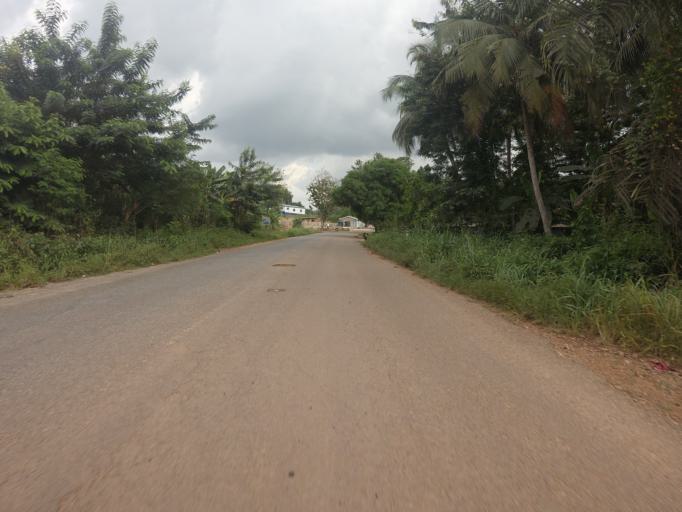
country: GH
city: Akropong
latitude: 5.9566
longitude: -0.1492
